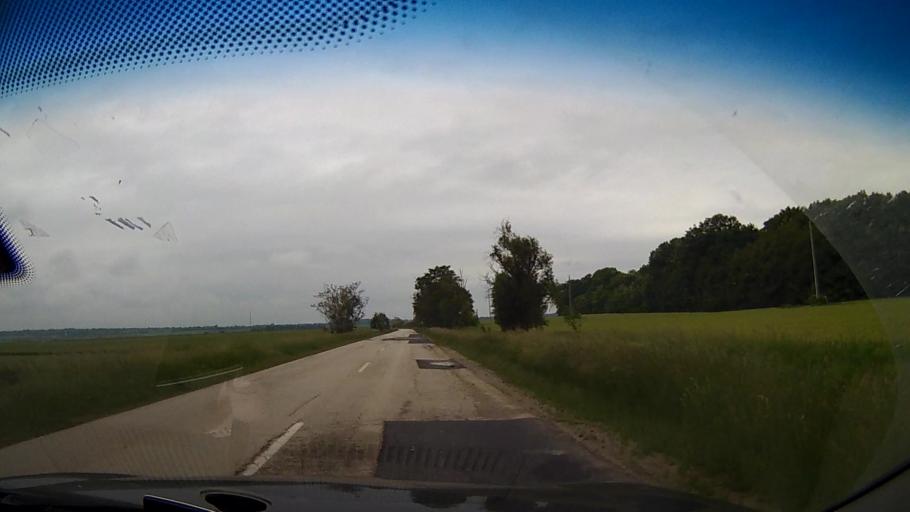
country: HU
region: Fejer
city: Many
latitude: 47.5290
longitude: 18.6673
